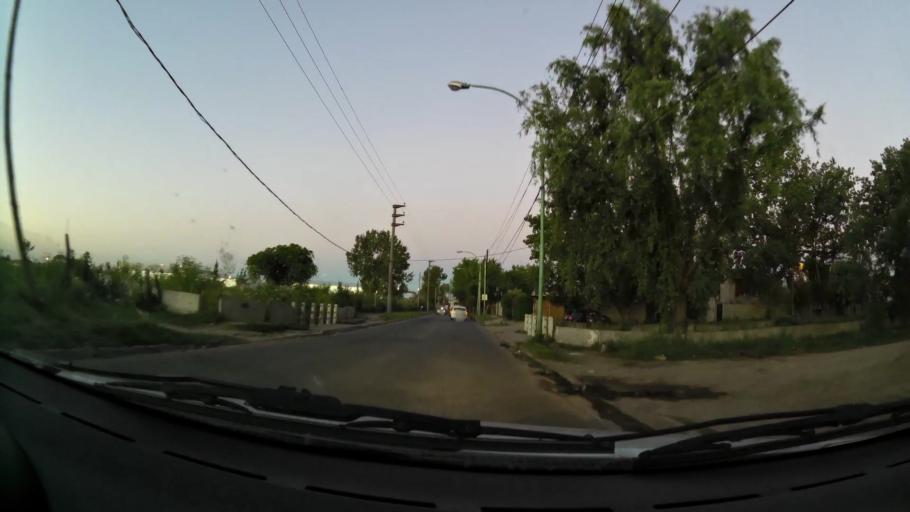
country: AR
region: Buenos Aires
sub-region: Partido de Quilmes
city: Quilmes
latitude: -34.8042
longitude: -58.1794
